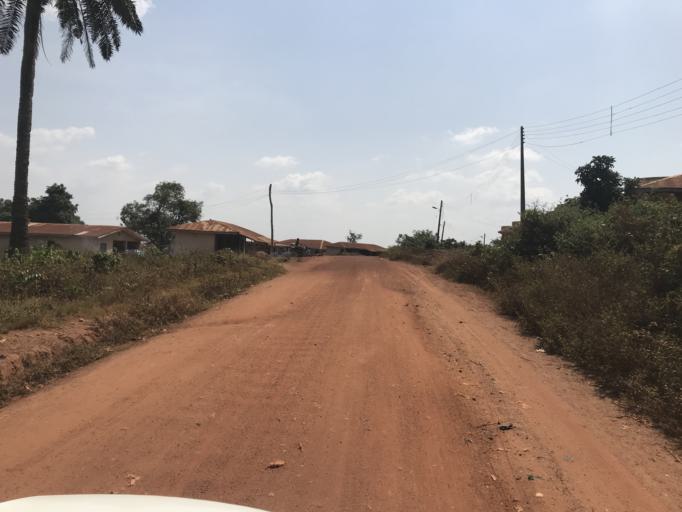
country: NG
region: Osun
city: Ifon
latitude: 7.8705
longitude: 4.4788
